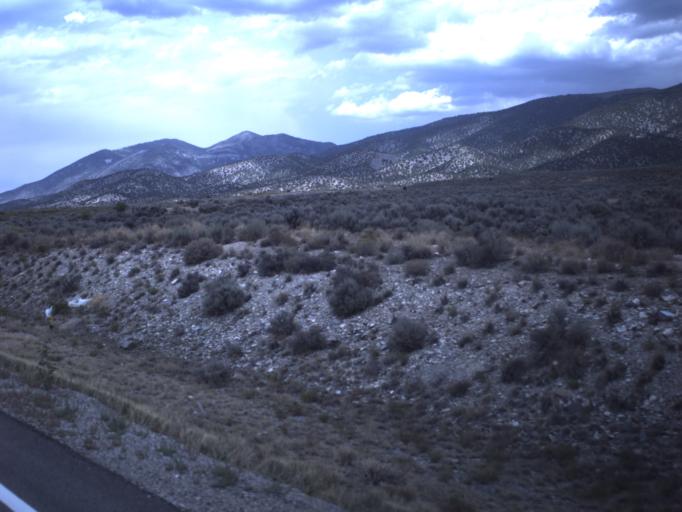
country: US
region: Utah
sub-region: Tooele County
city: Tooele
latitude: 40.2926
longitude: -112.2722
